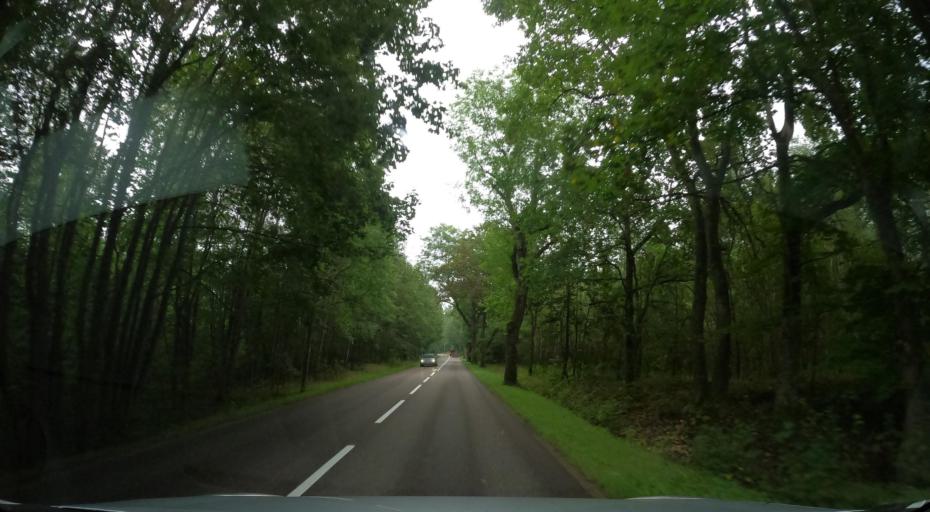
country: PL
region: Pomeranian Voivodeship
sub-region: Powiat wejherowski
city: Linia
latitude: 54.4604
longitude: 18.0496
